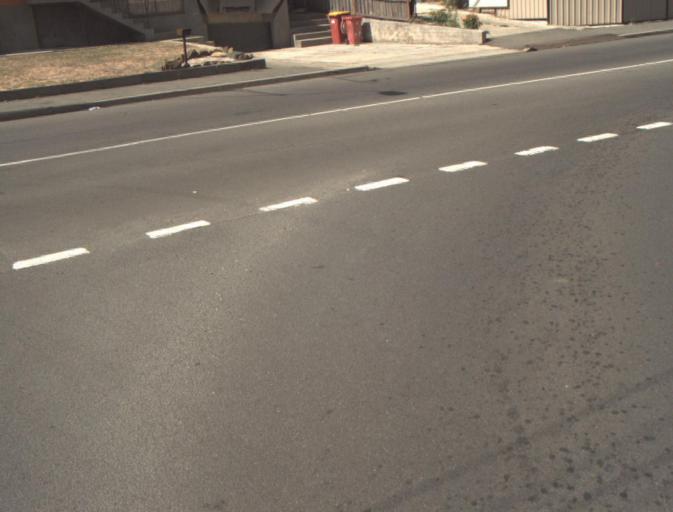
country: AU
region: Tasmania
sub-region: Launceston
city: Newstead
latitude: -41.4191
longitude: 147.1741
